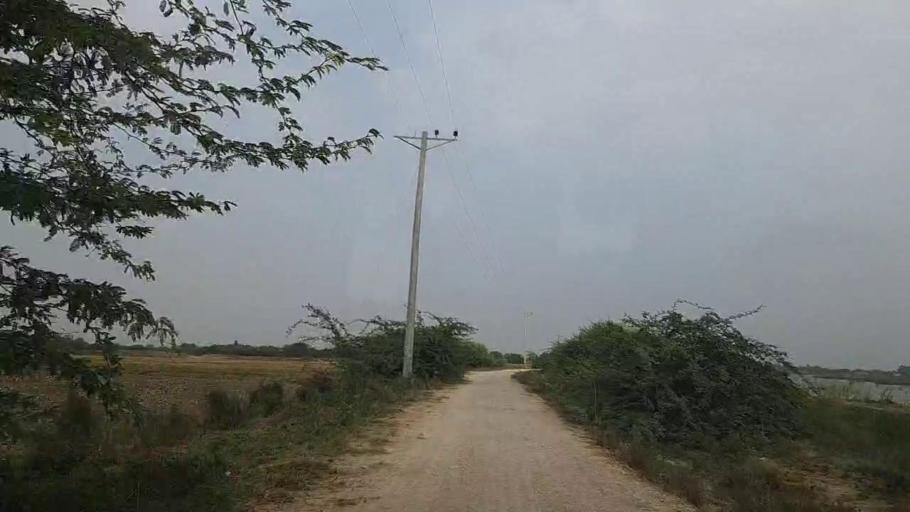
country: PK
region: Sindh
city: Mirpur Sakro
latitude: 24.6049
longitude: 67.7011
